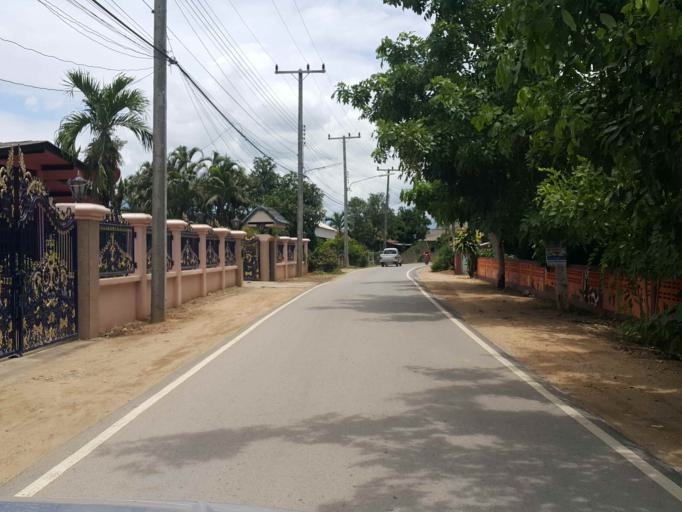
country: TH
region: Chiang Mai
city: Doi Lo
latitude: 18.4817
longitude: 98.8095
